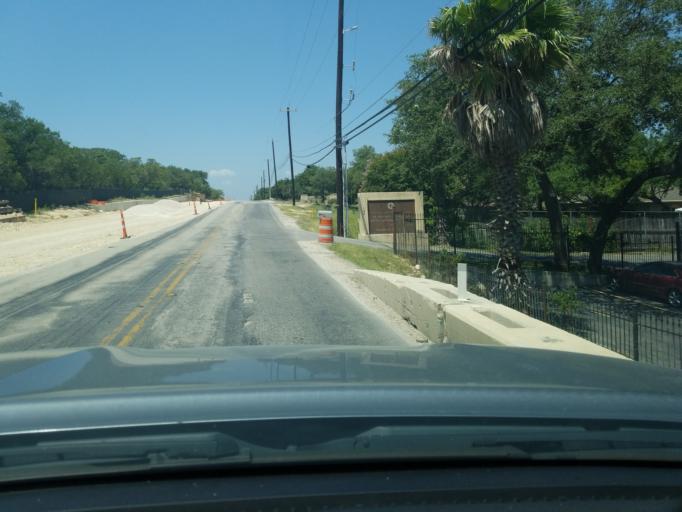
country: US
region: Texas
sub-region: Bexar County
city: Timberwood Park
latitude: 29.7083
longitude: -98.4937
